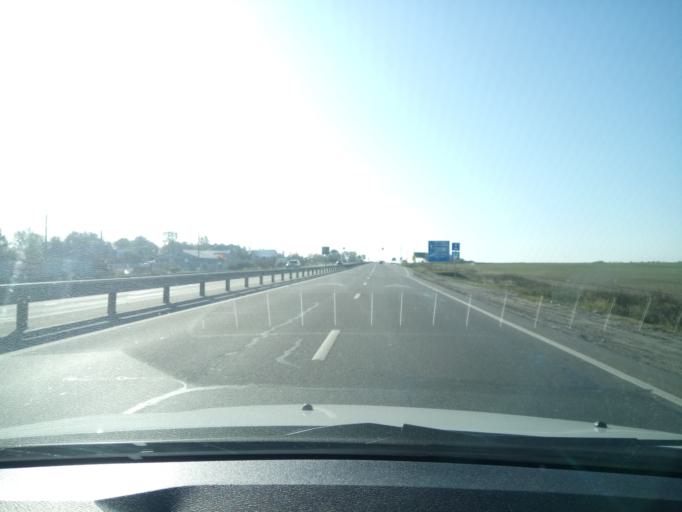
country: RU
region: Nizjnij Novgorod
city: Burevestnik
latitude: 56.1475
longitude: 43.9098
